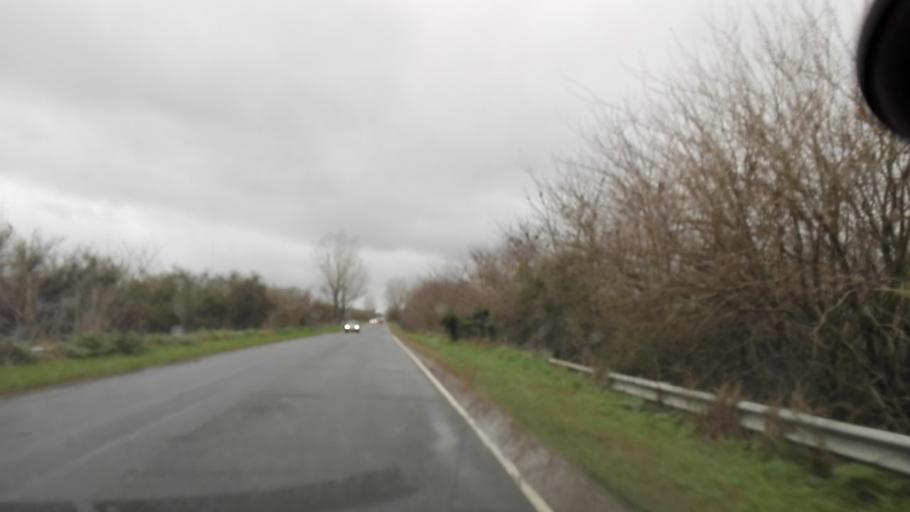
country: AR
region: Buenos Aires
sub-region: Partido de Brandsen
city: Brandsen
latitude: -35.1793
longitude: -58.2564
